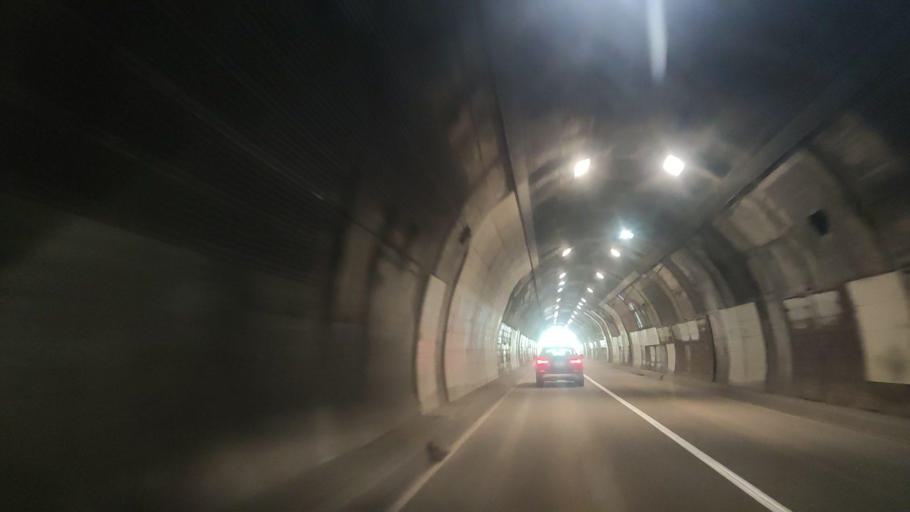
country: JP
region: Hokkaido
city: Date
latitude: 42.5637
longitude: 140.7402
